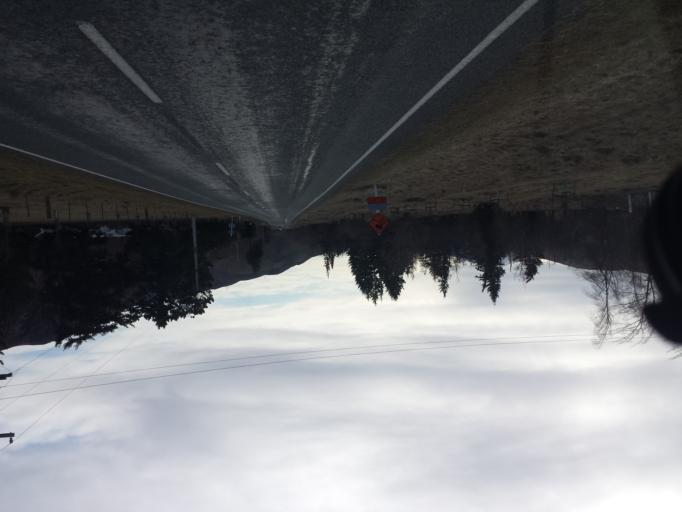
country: NZ
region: Canterbury
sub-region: Timaru District
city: Pleasant Point
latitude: -44.0869
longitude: 170.6556
